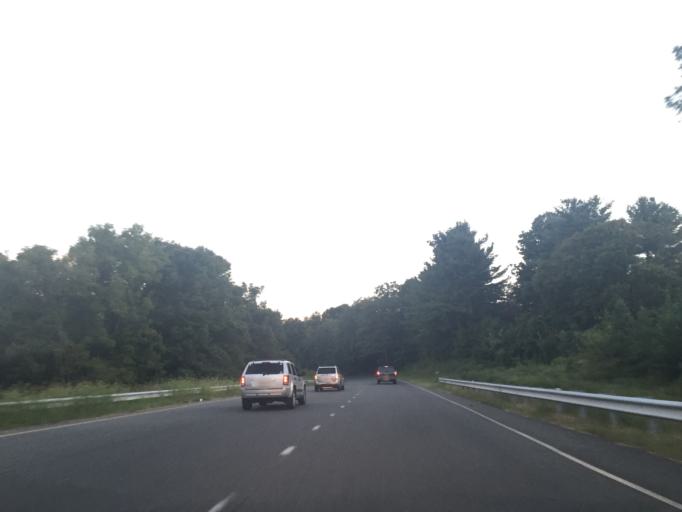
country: US
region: Maryland
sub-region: Harford County
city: Bel Air North
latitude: 39.5557
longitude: -76.3696
